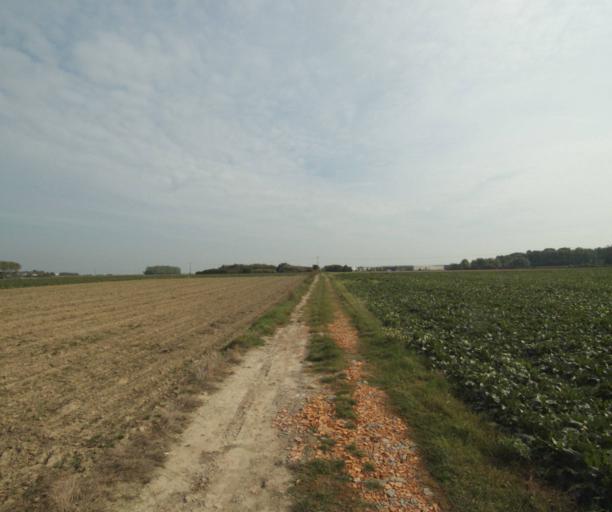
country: FR
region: Nord-Pas-de-Calais
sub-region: Departement du Nord
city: Templemars
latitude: 50.5610
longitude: 3.0503
